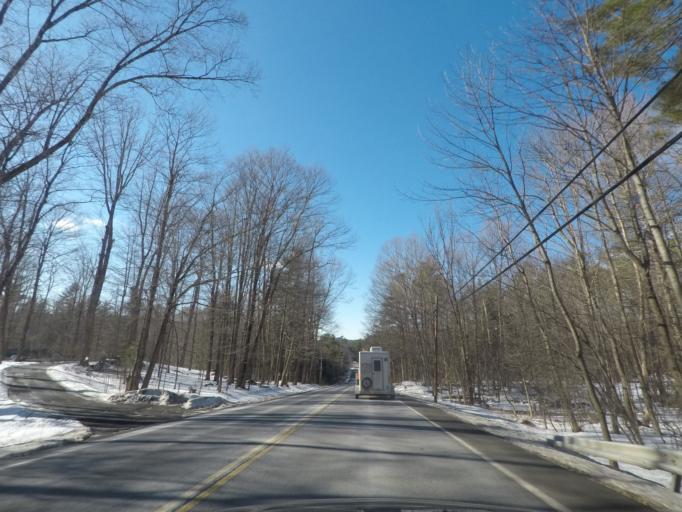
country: US
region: Massachusetts
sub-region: Berkshire County
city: Richmond
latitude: 42.4079
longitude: -73.4326
